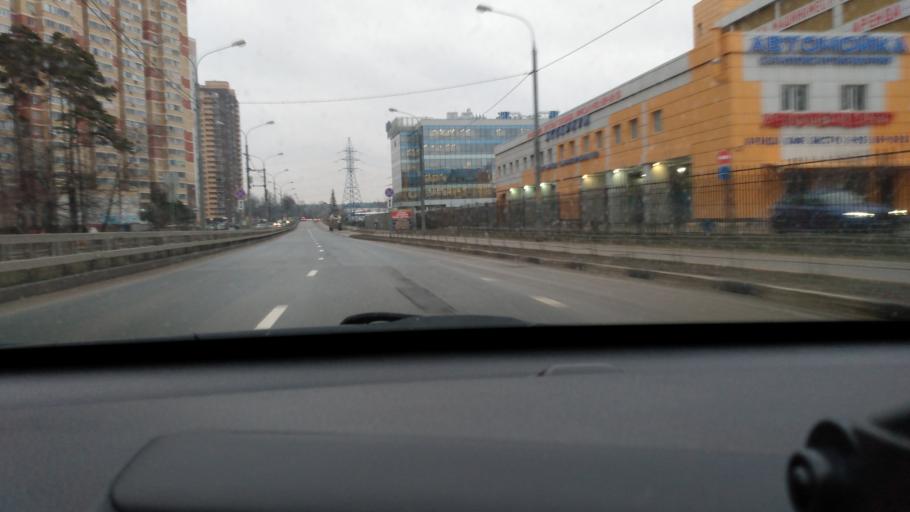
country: RU
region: Moskovskaya
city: Odintsovo
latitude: 55.6658
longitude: 37.2808
